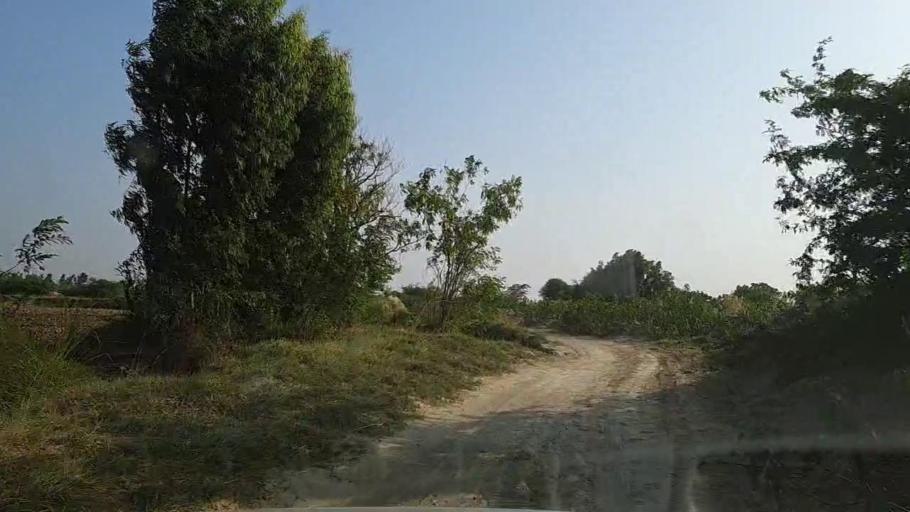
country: PK
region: Sindh
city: Mirpur Sakro
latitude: 24.5882
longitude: 67.6481
